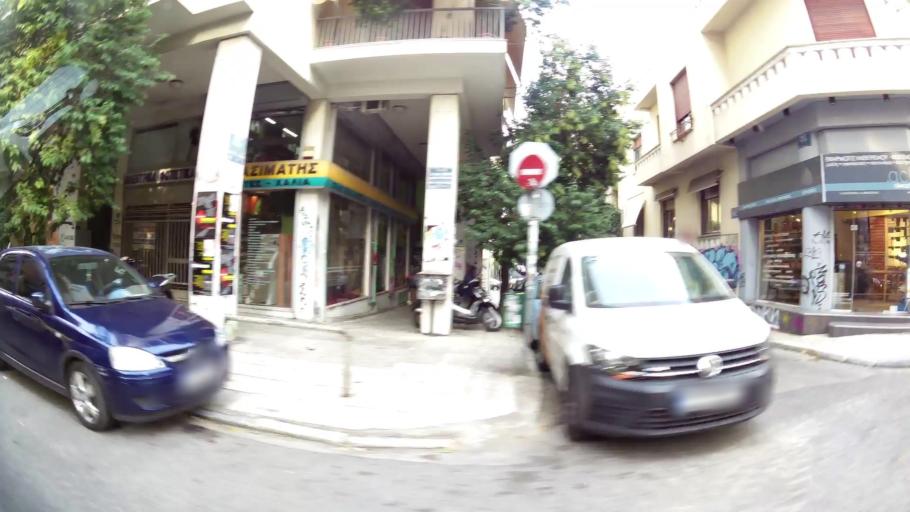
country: GR
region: Attica
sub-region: Nomarchia Athinas
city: Kipseli
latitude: 37.9854
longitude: 23.7381
